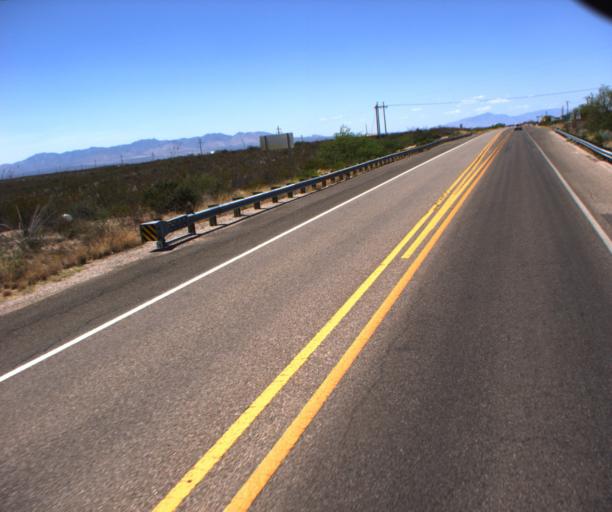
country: US
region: Arizona
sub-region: Cochise County
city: Tombstone
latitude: 31.7462
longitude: -110.0946
